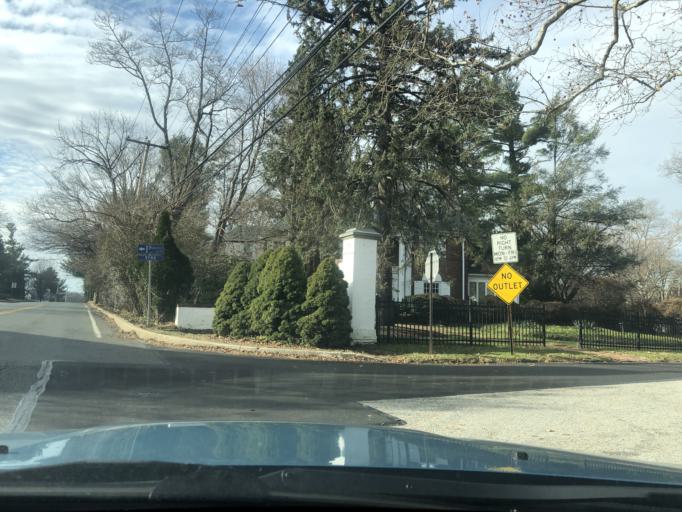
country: US
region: Pennsylvania
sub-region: Delaware County
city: Radnor
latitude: 40.0381
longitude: -75.3444
